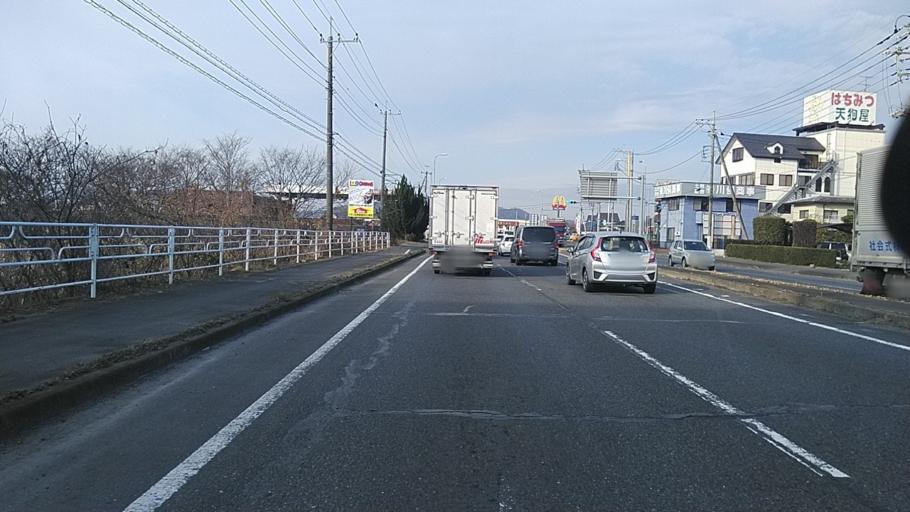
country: JP
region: Tochigi
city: Fujioka
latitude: 36.3143
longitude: 139.6662
